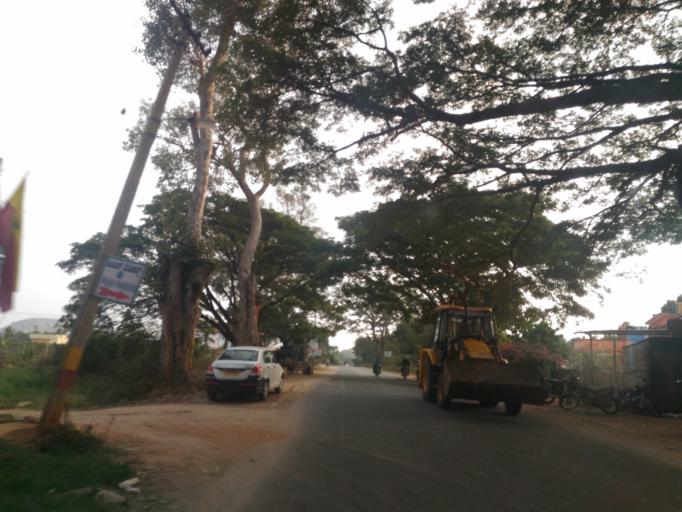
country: IN
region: Karnataka
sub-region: Bangalore Rural
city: Devanhalli
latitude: 13.3272
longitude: 77.6920
